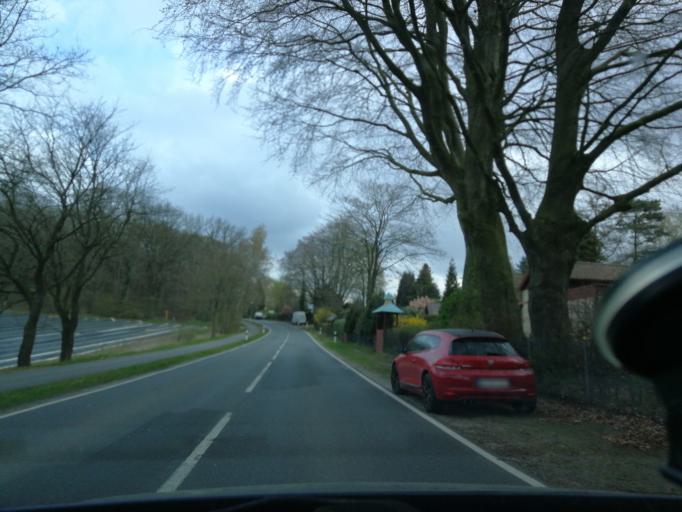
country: DE
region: Lower Saxony
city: Seevetal
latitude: 53.4400
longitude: 9.9163
